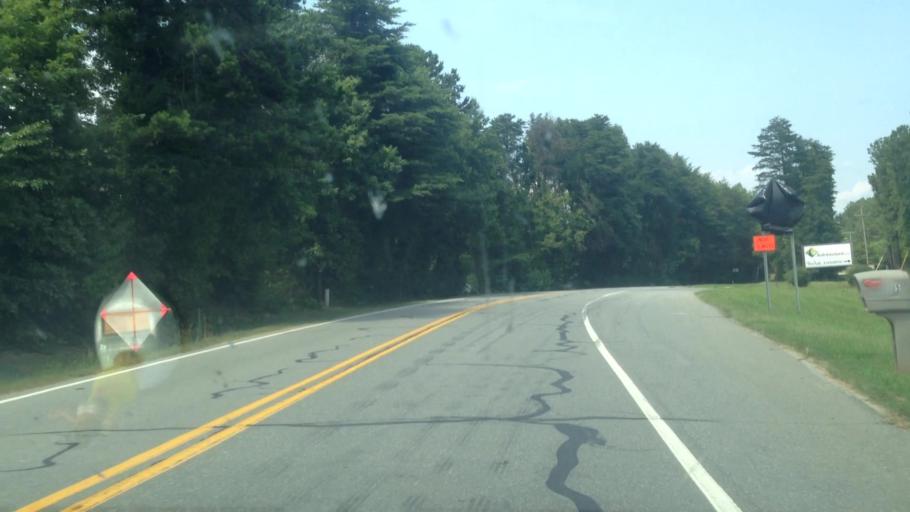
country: US
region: North Carolina
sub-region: Stokes County
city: Walnut Cove
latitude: 36.2872
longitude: -80.0671
